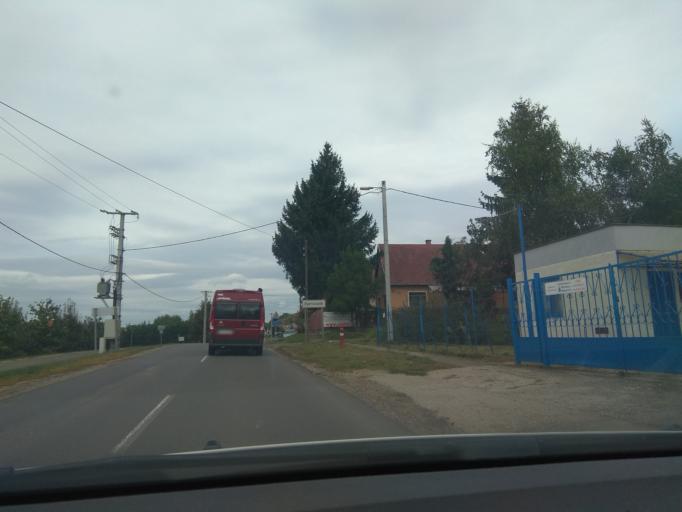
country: HU
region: Heves
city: Egerszalok
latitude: 47.8640
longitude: 20.3277
